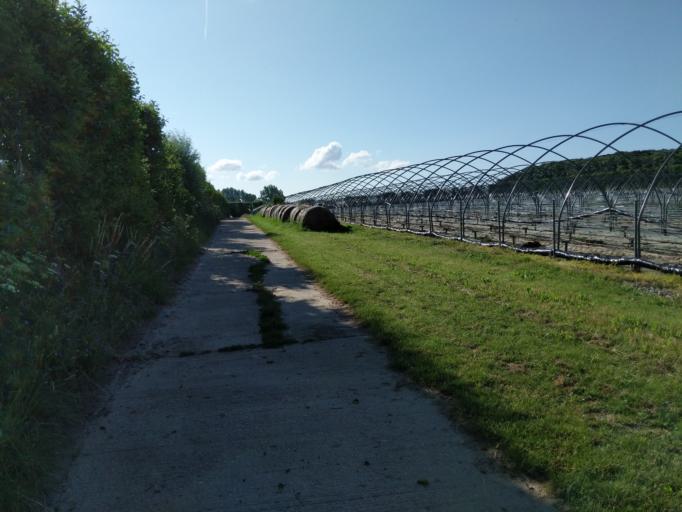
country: GB
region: England
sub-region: Kent
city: Faversham
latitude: 51.3306
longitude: 0.9261
